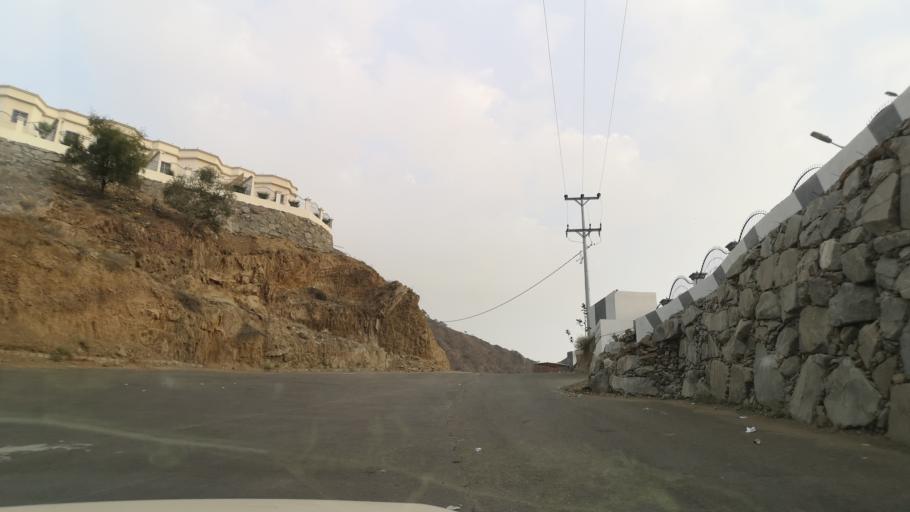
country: YE
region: Sa'dah
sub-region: Monabbih
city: Suq al Khamis
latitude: 17.3236
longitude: 43.1478
